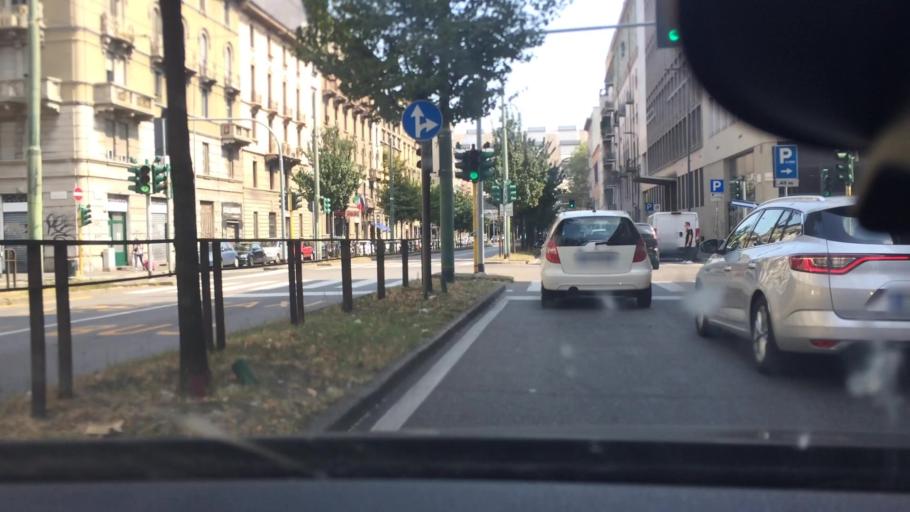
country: IT
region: Lombardy
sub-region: Citta metropolitana di Milano
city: Milano
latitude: 45.4891
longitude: 9.2020
